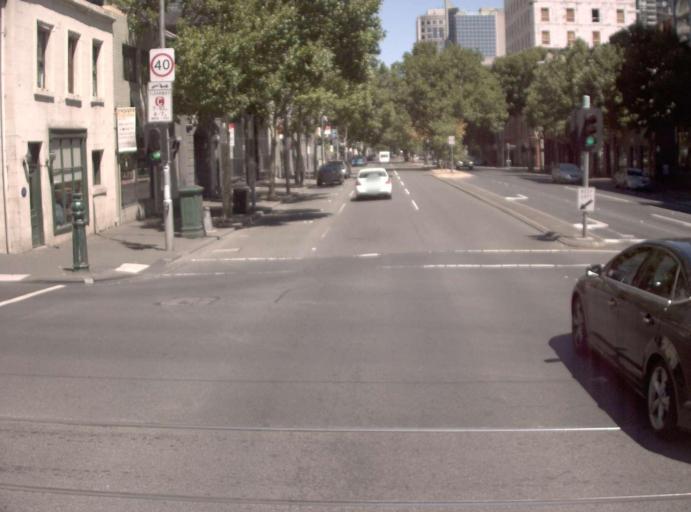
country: AU
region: Victoria
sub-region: Melbourne
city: Docklands
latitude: -37.8124
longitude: 144.9540
